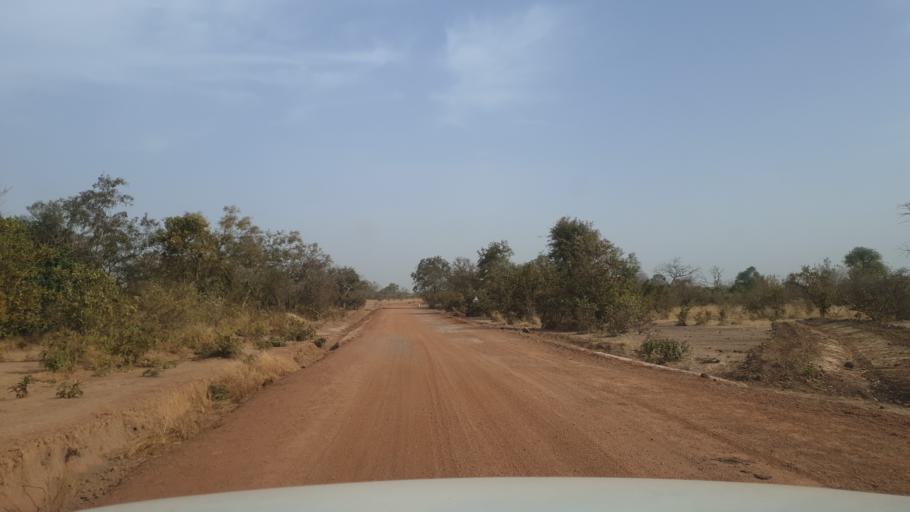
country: ML
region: Koulikoro
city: Kolokani
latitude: 13.3085
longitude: -8.2794
